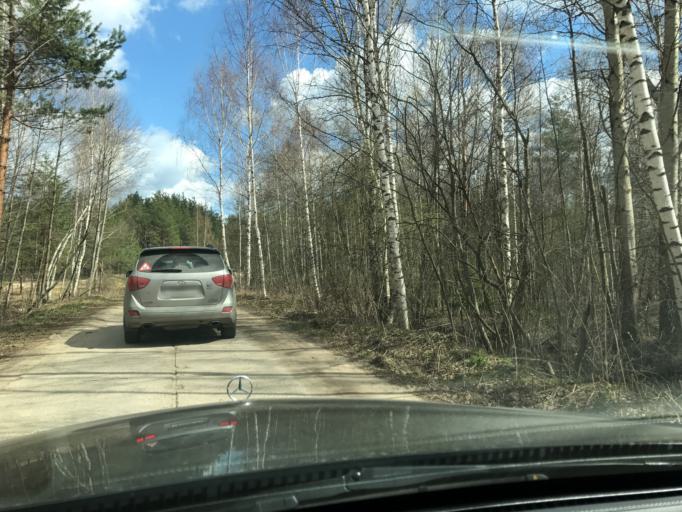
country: RU
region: Vladimir
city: Pokrov
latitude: 55.8605
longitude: 39.2058
